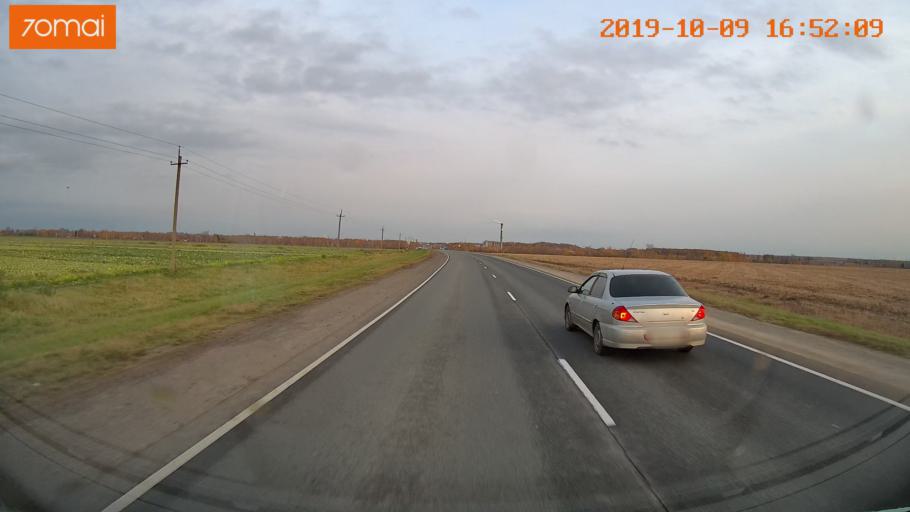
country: RU
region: Ivanovo
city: Privolzhsk
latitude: 57.3823
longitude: 41.2394
